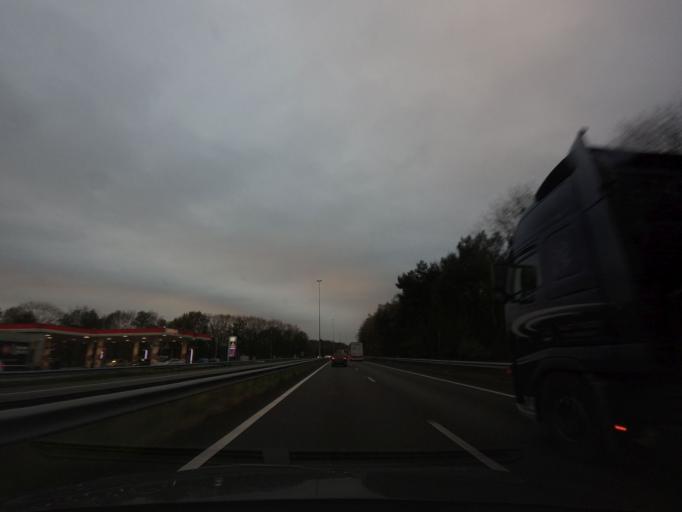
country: NL
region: North Brabant
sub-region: Gemeente Oosterhout
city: Oosterhout
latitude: 51.6122
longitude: 4.8562
